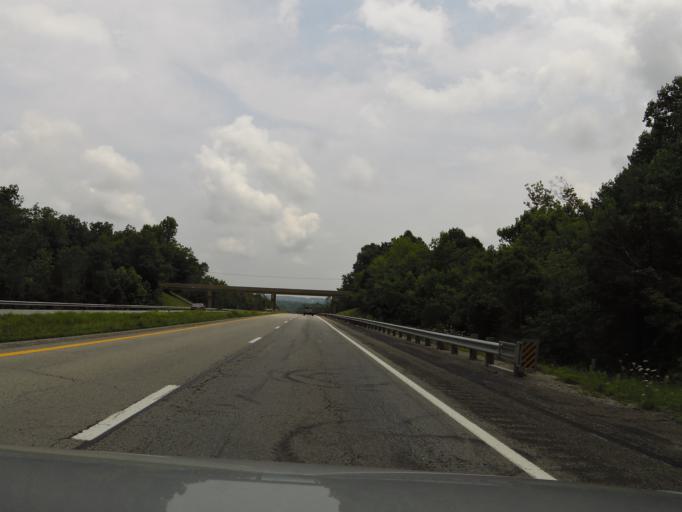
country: US
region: Kentucky
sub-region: Grayson County
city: Leitchfield
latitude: 37.5560
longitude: -86.0804
